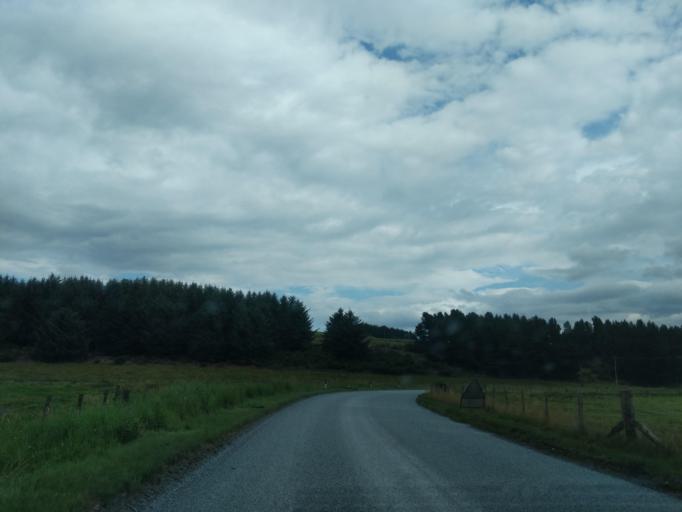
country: GB
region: Scotland
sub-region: Highland
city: Grantown on Spey
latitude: 57.3077
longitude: -3.7023
